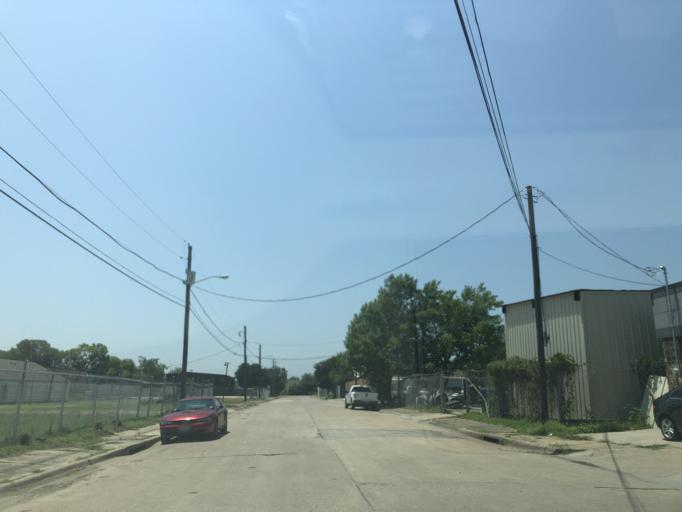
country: US
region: Texas
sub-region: Dallas County
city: Dallas
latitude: 32.8048
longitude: -96.8502
